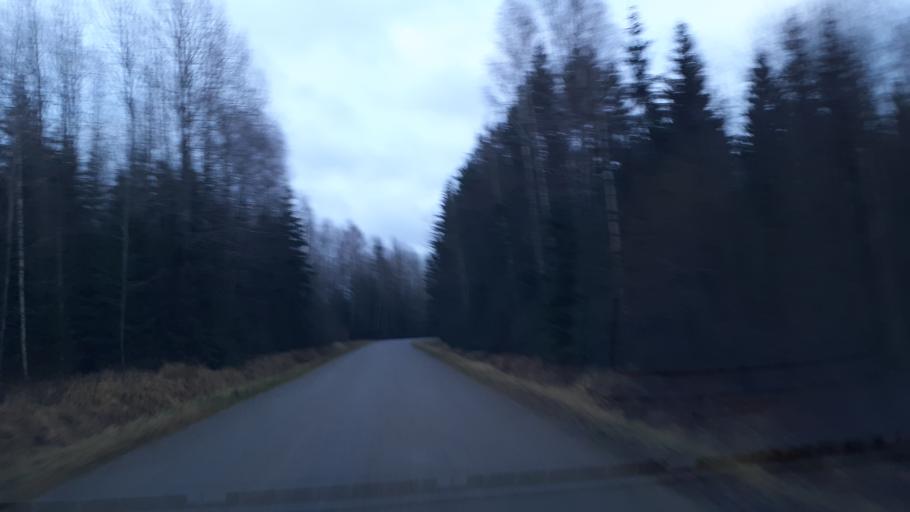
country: LV
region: Kuldigas Rajons
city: Kuldiga
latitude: 57.0361
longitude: 22.1539
